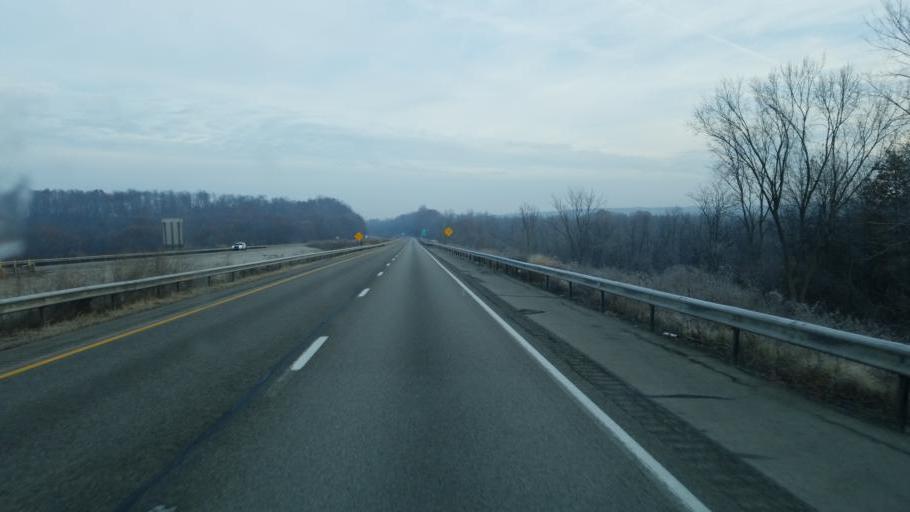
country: US
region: Pennsylvania
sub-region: Mercer County
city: Mercer
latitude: 41.2284
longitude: -80.1624
